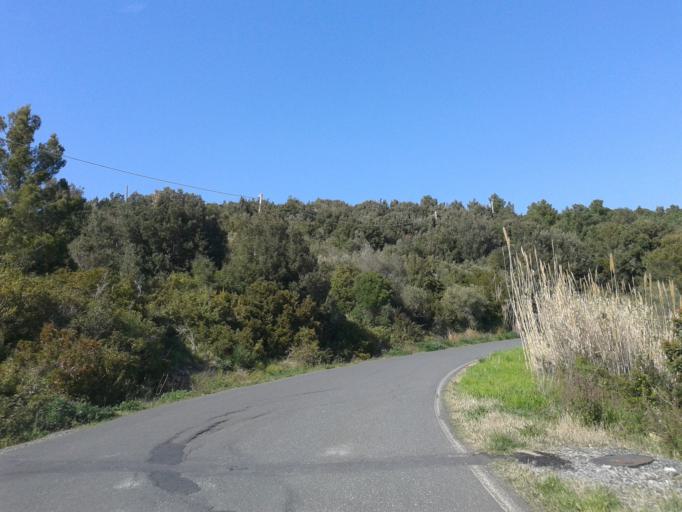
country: IT
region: Tuscany
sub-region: Provincia di Livorno
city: Quercianella
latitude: 43.4560
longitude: 10.4046
